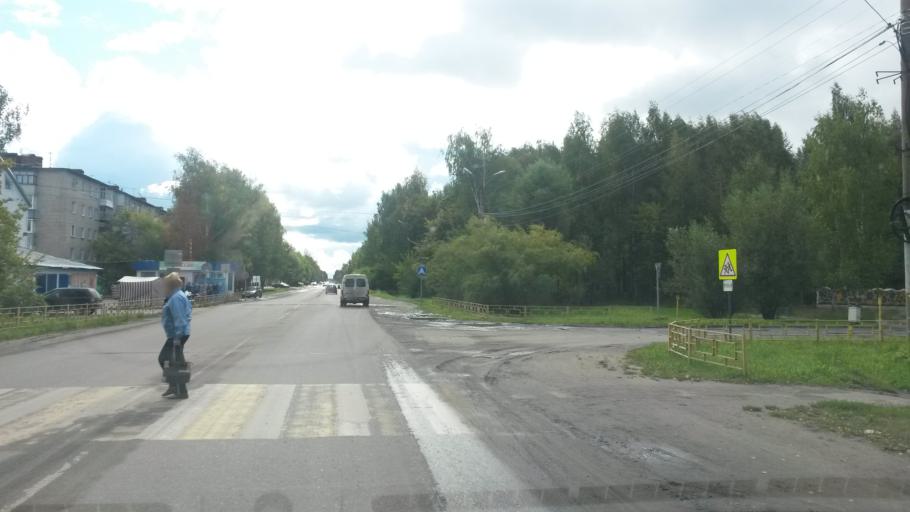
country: RU
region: Ivanovo
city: Zavolzhsk
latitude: 57.4902
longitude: 42.1390
